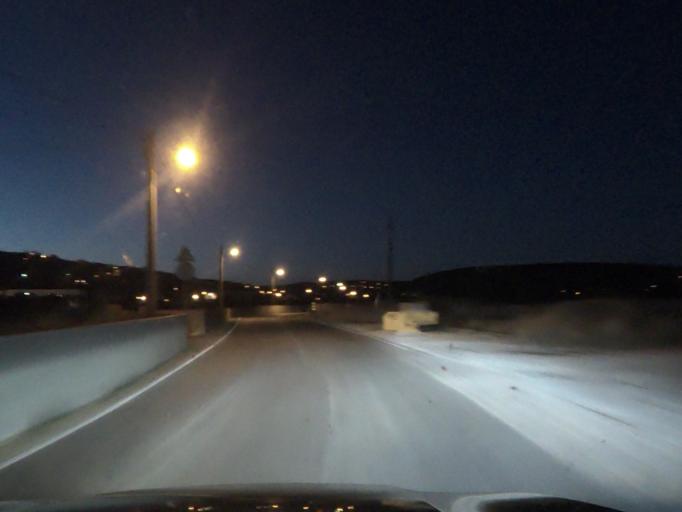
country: PT
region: Faro
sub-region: Loule
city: Loule
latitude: 37.1406
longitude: -8.0102
